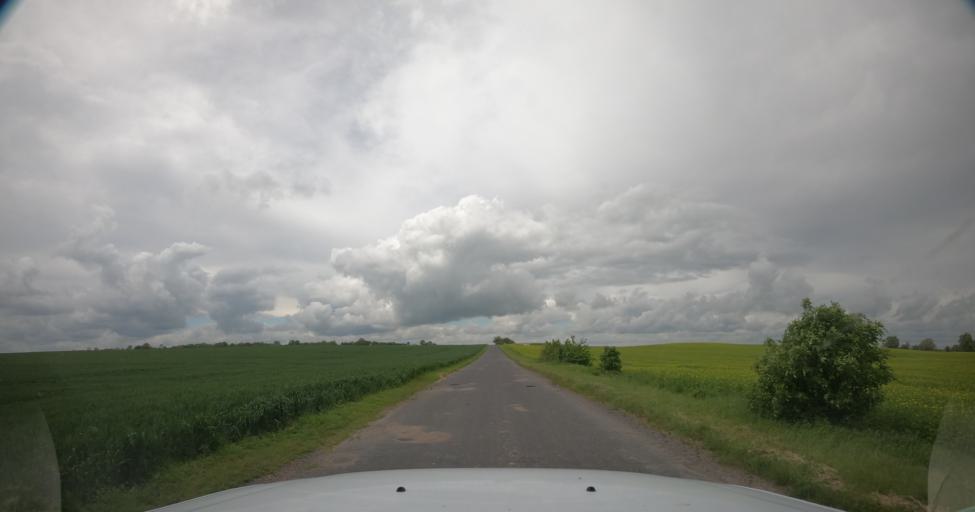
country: PL
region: West Pomeranian Voivodeship
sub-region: Powiat pyrzycki
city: Kozielice
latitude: 53.0781
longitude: 14.8696
